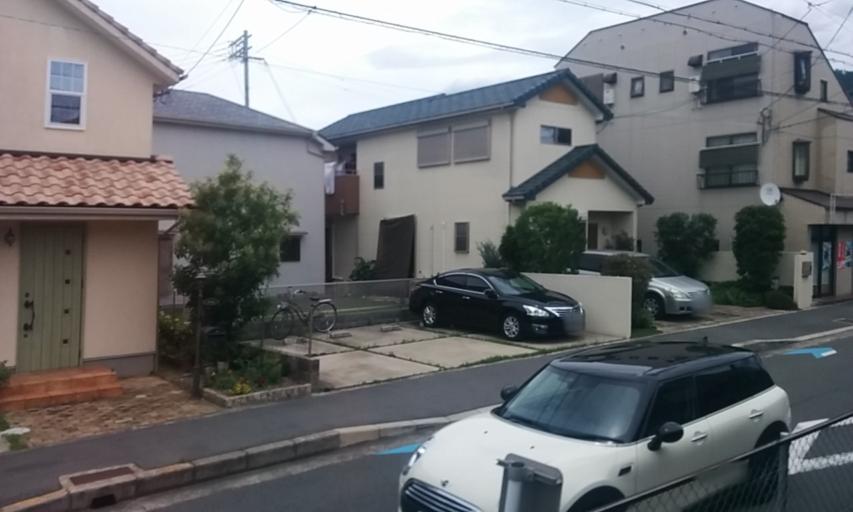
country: JP
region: Osaka
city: Mino
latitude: 34.8292
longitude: 135.4669
